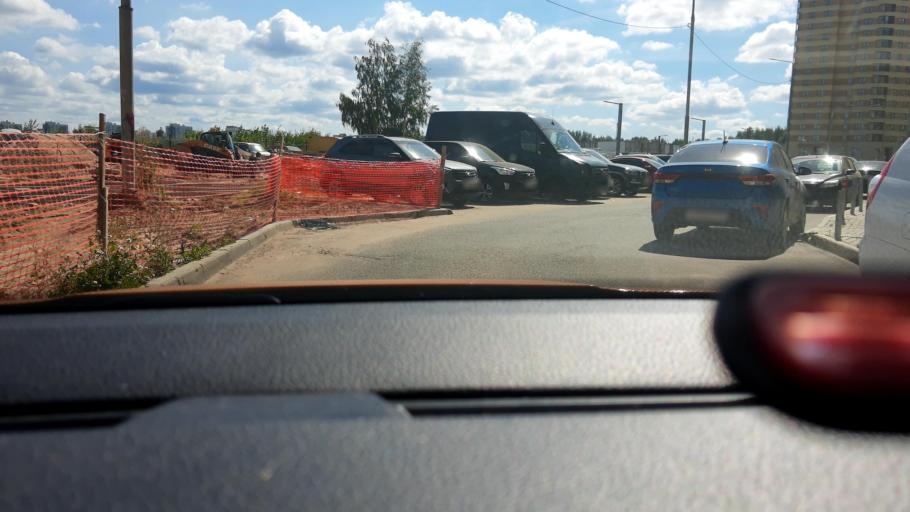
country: RU
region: Moskovskaya
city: Mytishchi
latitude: 55.9269
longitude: 37.7297
